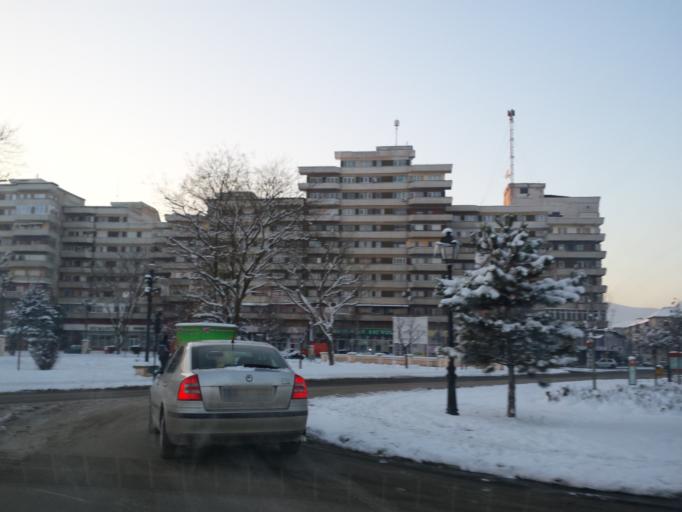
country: RO
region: Alba
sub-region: Municipiul Alba Iulia
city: Alba Iulia
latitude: 46.0700
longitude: 23.5661
